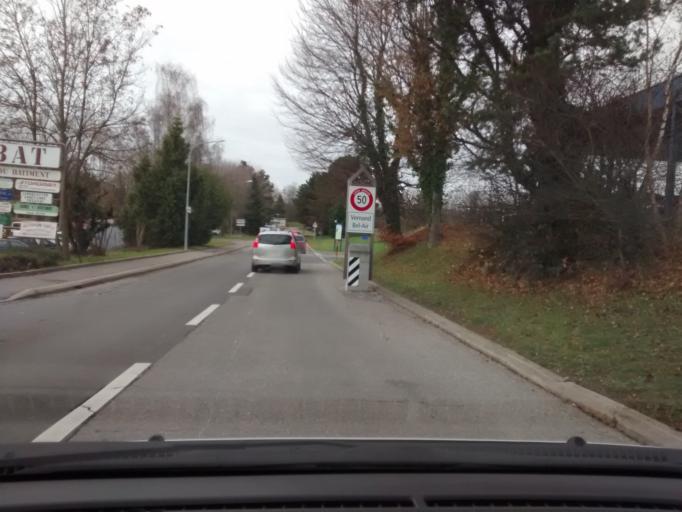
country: CH
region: Vaud
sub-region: Lausanne District
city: Cheseaux
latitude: 46.5782
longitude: 6.6053
